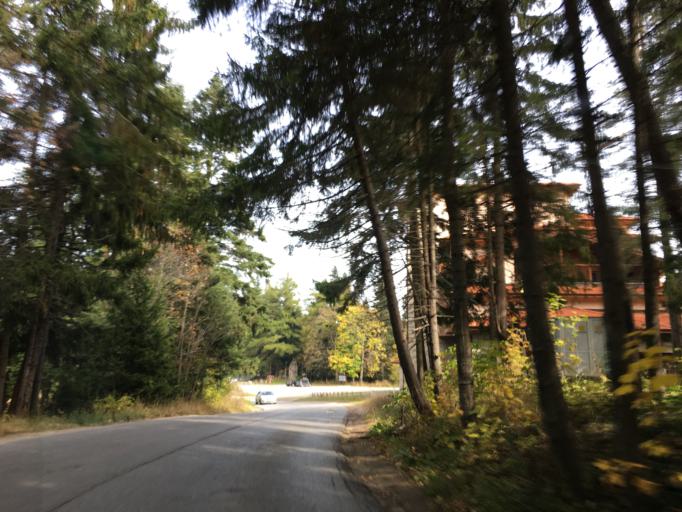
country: BG
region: Sofiya
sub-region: Obshtina Samokov
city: Samokov
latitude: 42.2714
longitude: 23.6159
